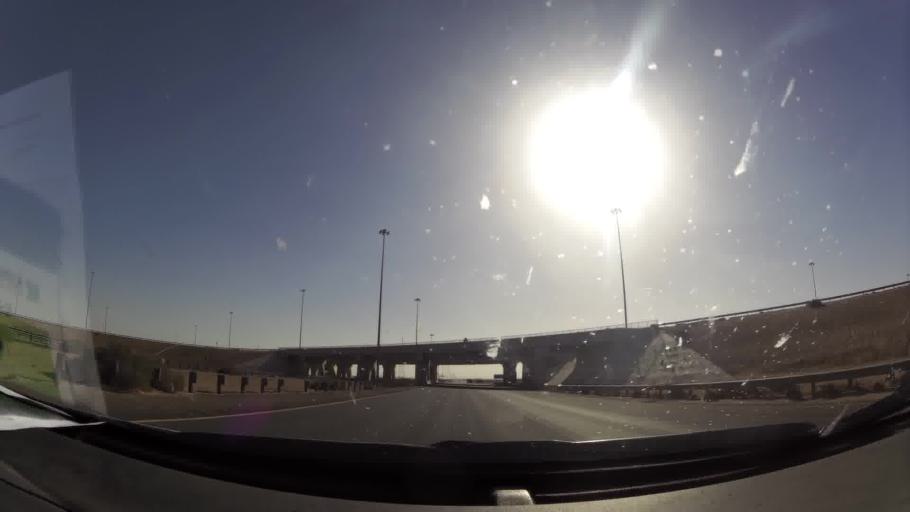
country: KW
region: Al Asimah
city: Kuwait City
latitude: 29.6098
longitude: 47.9147
